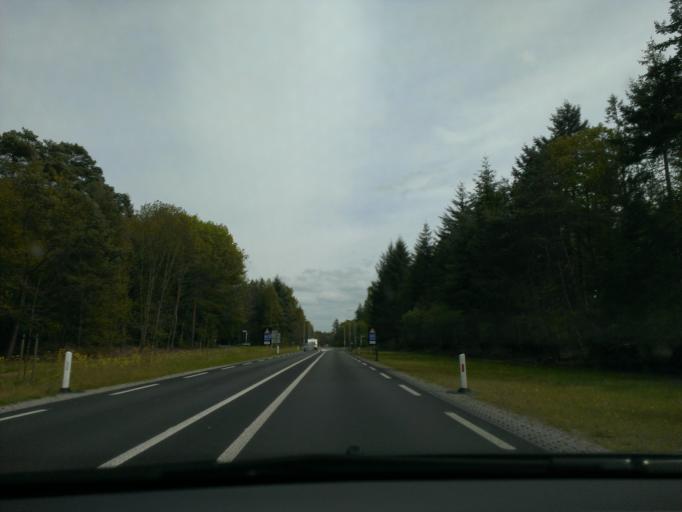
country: NL
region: Gelderland
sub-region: Gemeente Nunspeet
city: Nunspeet
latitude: 52.3741
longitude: 5.8252
